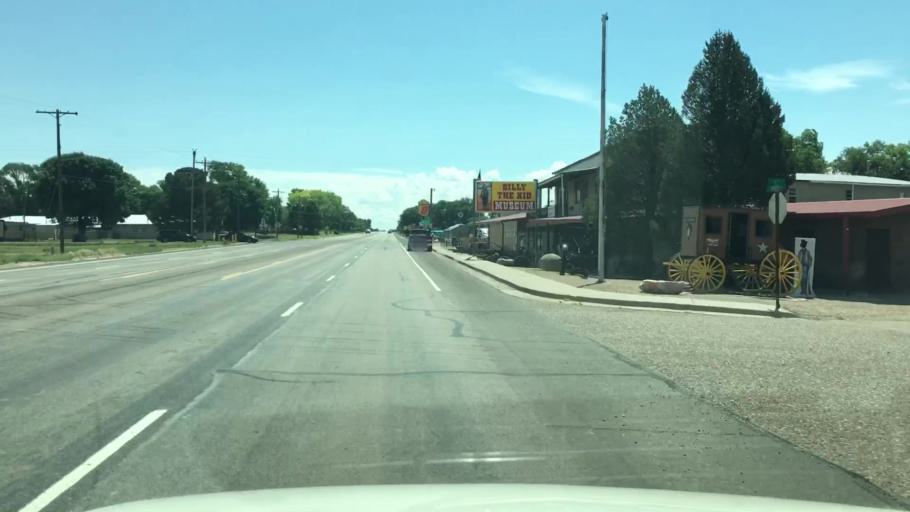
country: US
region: New Mexico
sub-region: De Baca County
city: Fort Sumner
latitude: 34.4667
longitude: -104.2298
